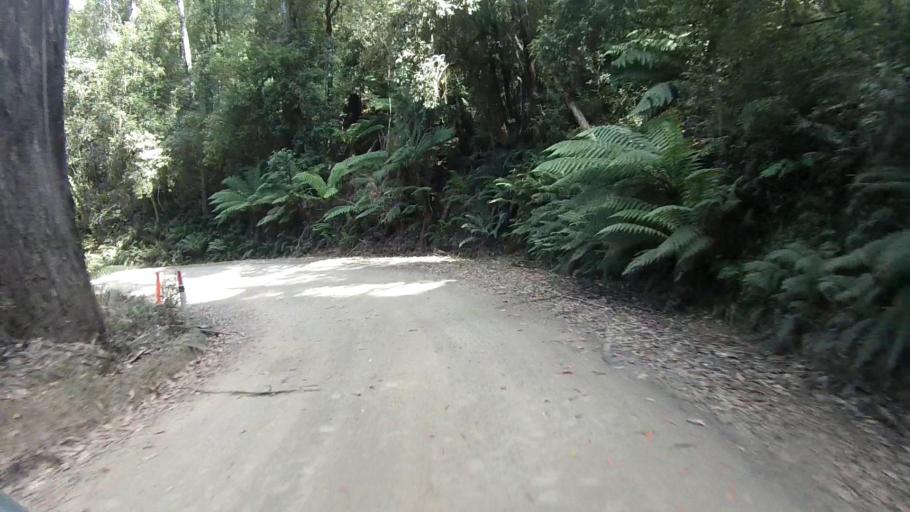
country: AU
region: Tasmania
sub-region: Derwent Valley
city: New Norfolk
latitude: -42.6756
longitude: 146.7042
